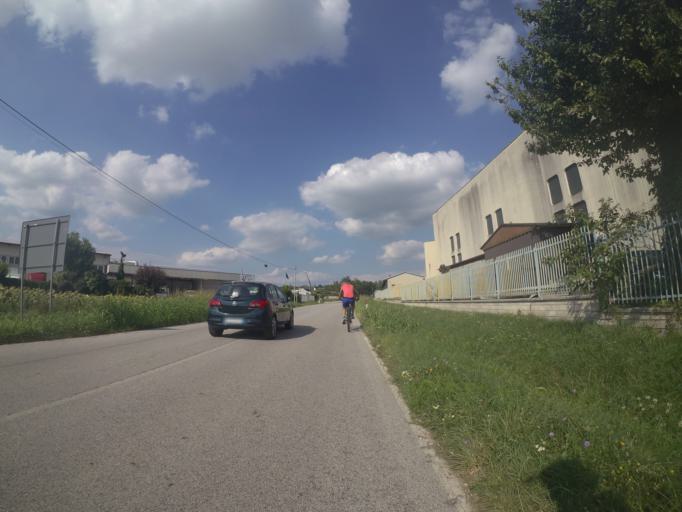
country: IT
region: Friuli Venezia Giulia
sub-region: Provincia di Udine
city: Fagagna
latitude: 46.0986
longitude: 13.0933
